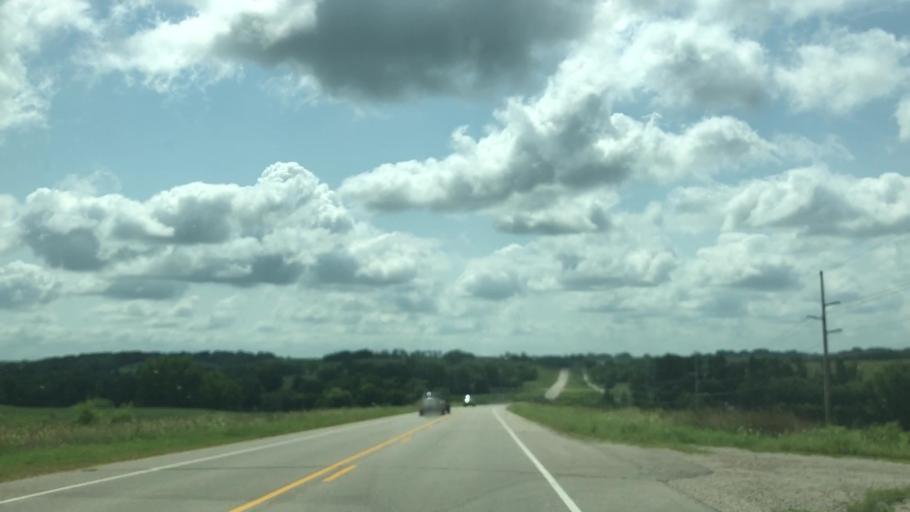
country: US
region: Iowa
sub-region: Marshall County
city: Marshalltown
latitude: 42.0246
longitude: -92.9602
